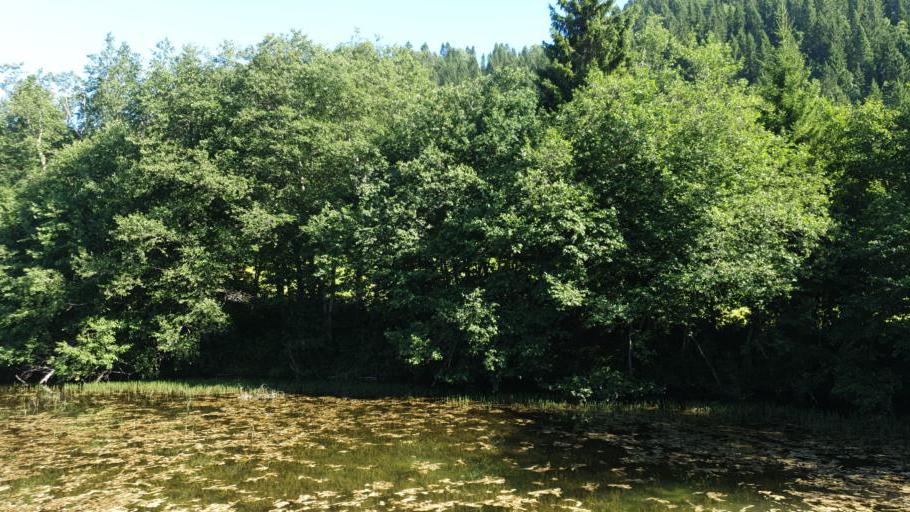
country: NO
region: Sor-Trondelag
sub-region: Orkdal
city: Orkanger
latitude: 63.1945
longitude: 9.7857
